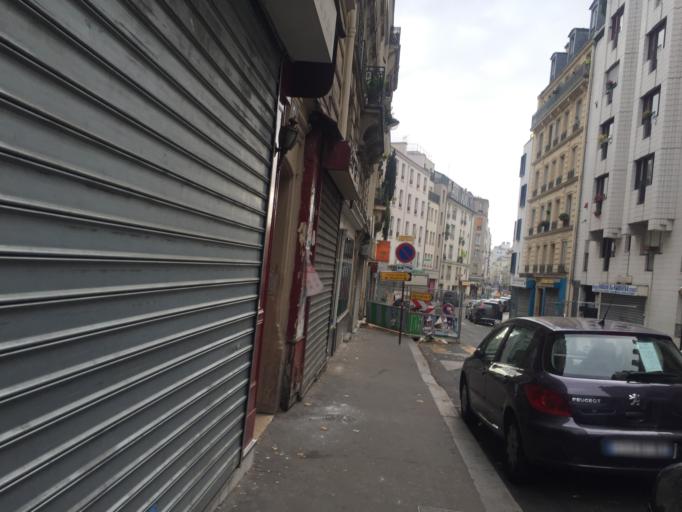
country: FR
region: Ile-de-France
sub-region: Paris
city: Saint-Ouen
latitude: 48.8906
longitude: 2.3501
